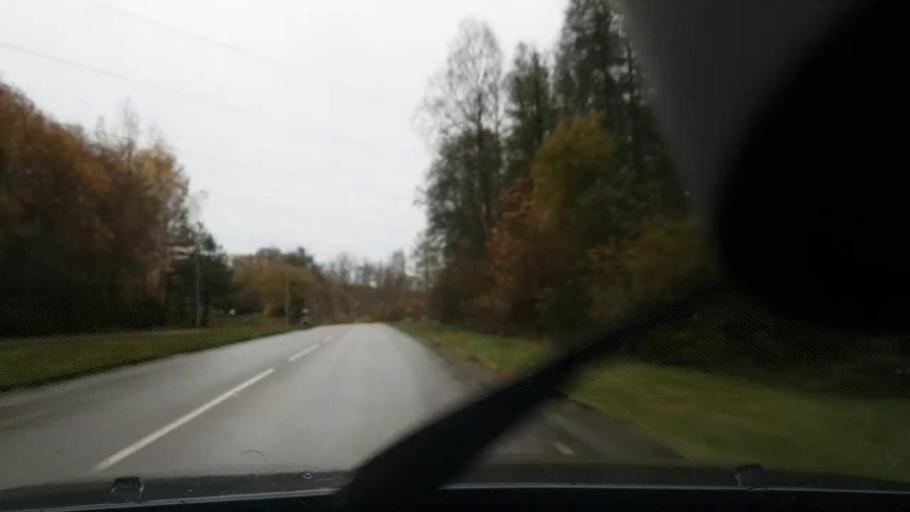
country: SE
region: Vaestra Goetaland
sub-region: Molndal
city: Lindome
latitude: 57.5987
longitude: 12.0829
